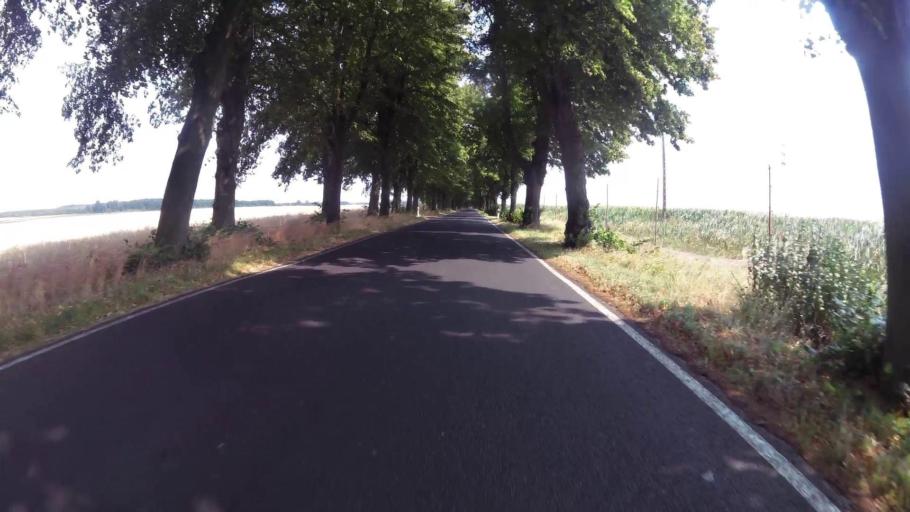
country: PL
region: West Pomeranian Voivodeship
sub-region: Powiat gryfinski
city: Mieszkowice
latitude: 52.8236
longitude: 14.4703
